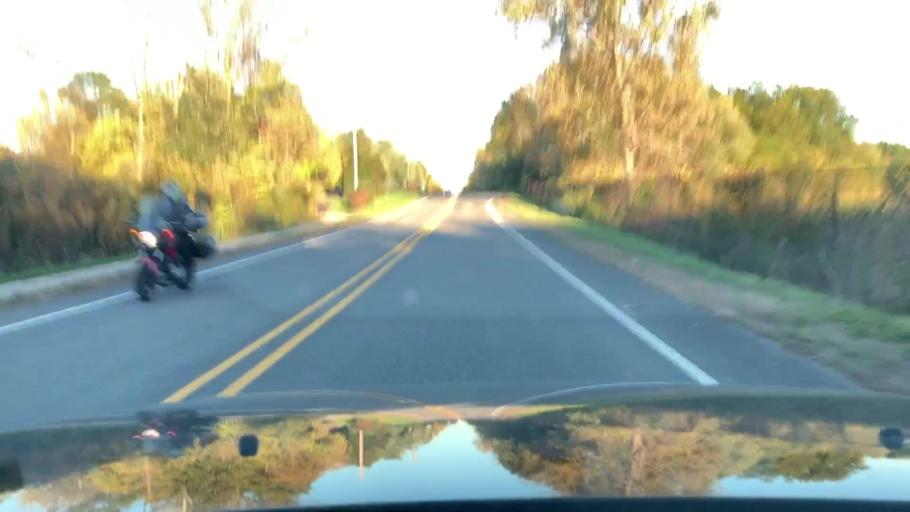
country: US
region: Michigan
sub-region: Kent County
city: East Grand Rapids
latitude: 42.9844
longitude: -85.5830
